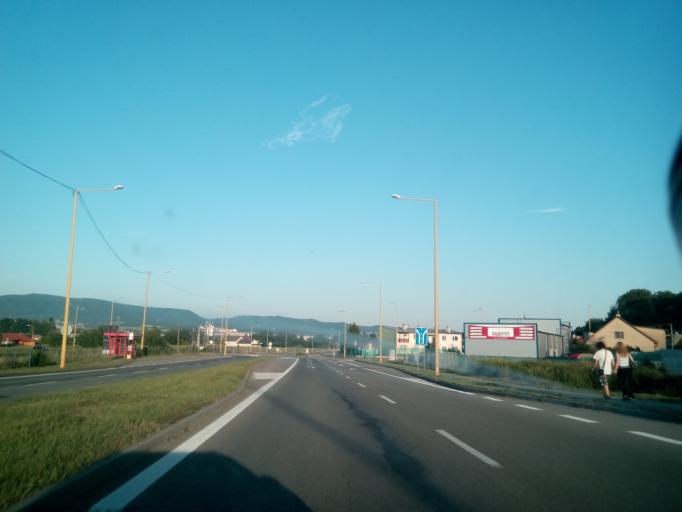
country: SK
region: Presovsky
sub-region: Okres Presov
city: Presov
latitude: 48.9836
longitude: 21.2329
